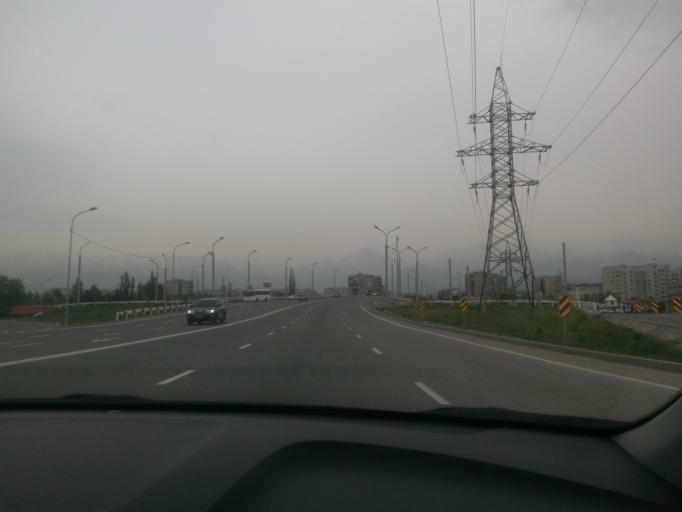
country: KZ
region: Almaty Qalasy
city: Almaty
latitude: 43.2458
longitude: 76.8268
